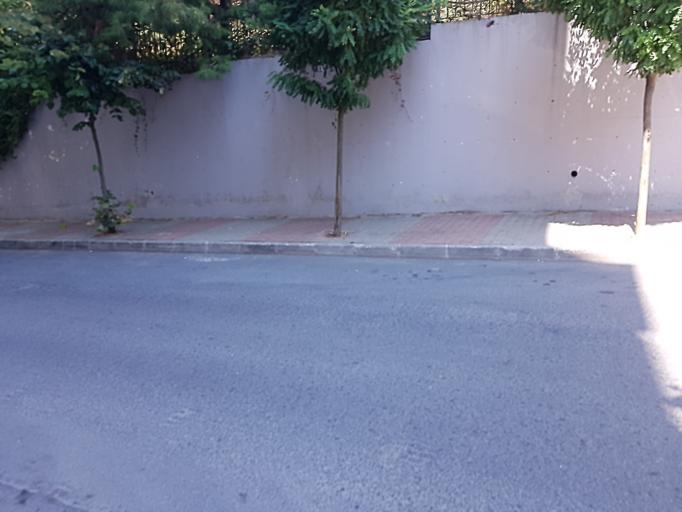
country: TR
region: Istanbul
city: Sisli
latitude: 41.0713
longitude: 29.0088
